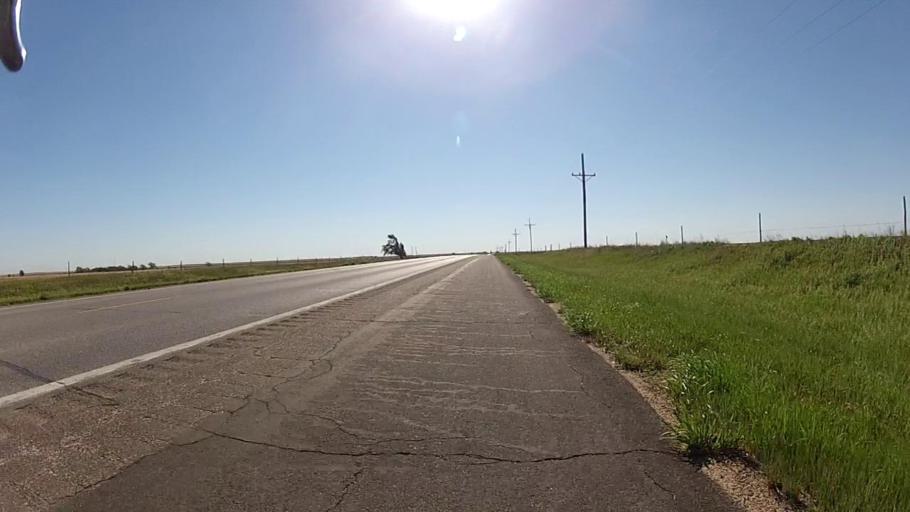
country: US
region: Kansas
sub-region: Ford County
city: Dodge City
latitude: 37.5863
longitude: -99.6746
